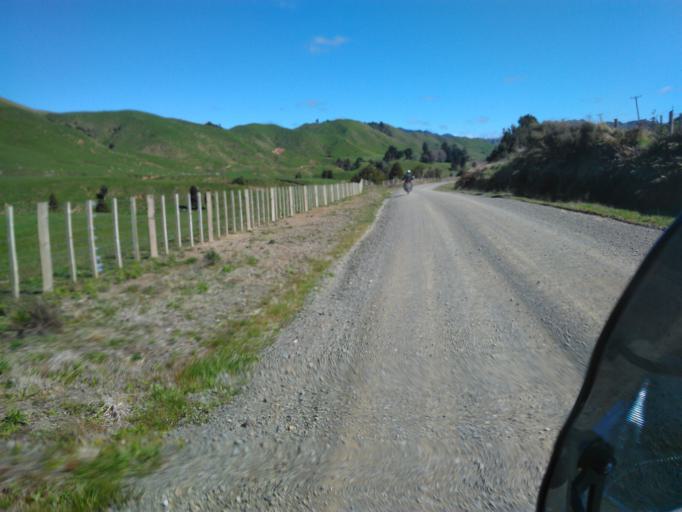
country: NZ
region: Bay of Plenty
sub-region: Opotiki District
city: Opotiki
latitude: -38.3013
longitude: 177.5593
